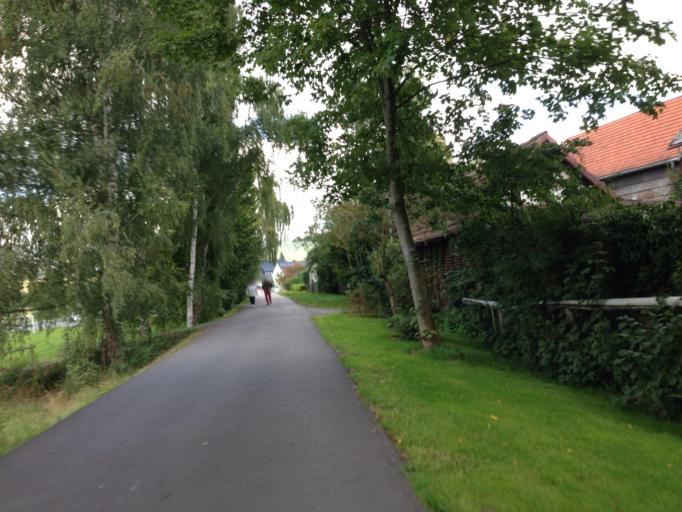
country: DE
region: Hesse
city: Battenberg
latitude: 51.0181
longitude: 8.6565
